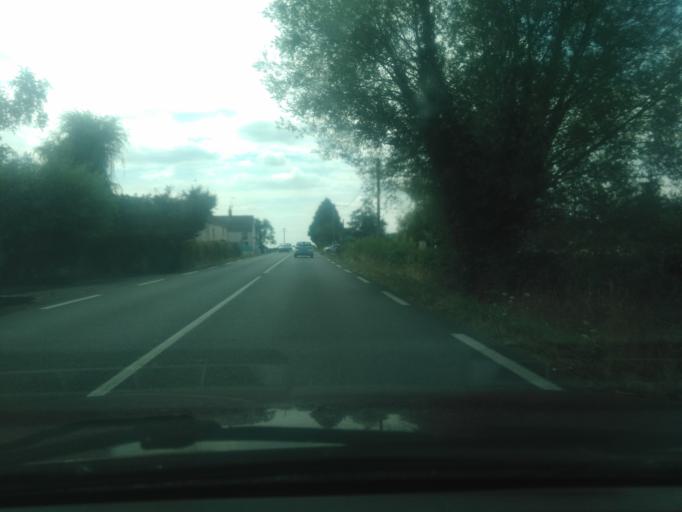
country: FR
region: Bourgogne
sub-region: Departement de la Nievre
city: Saint-Leger-des-Vignes
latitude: 46.8560
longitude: 3.3673
